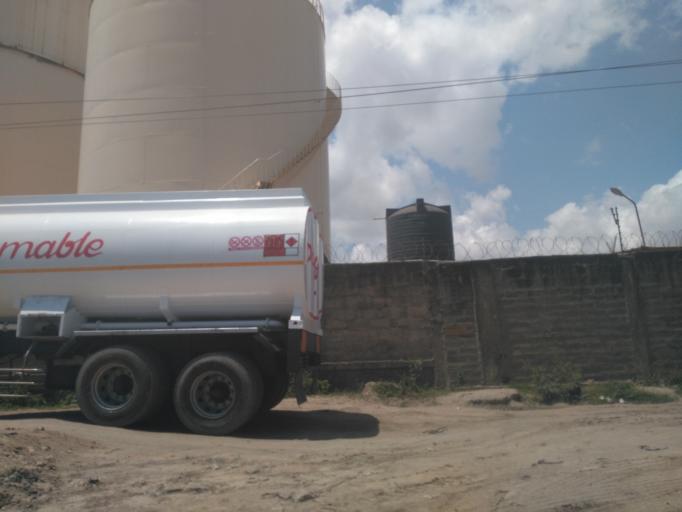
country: TZ
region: Dar es Salaam
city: Dar es Salaam
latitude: -6.8402
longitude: 39.2915
